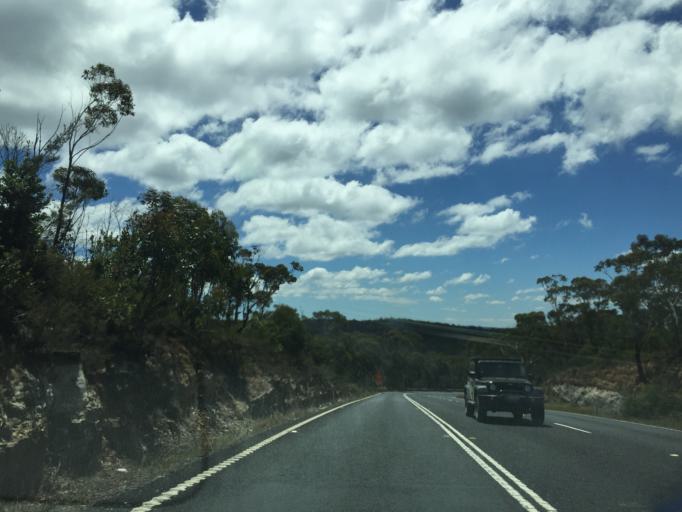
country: AU
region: New South Wales
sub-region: Blue Mountains Municipality
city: Blackheath
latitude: -33.5621
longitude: 150.3436
